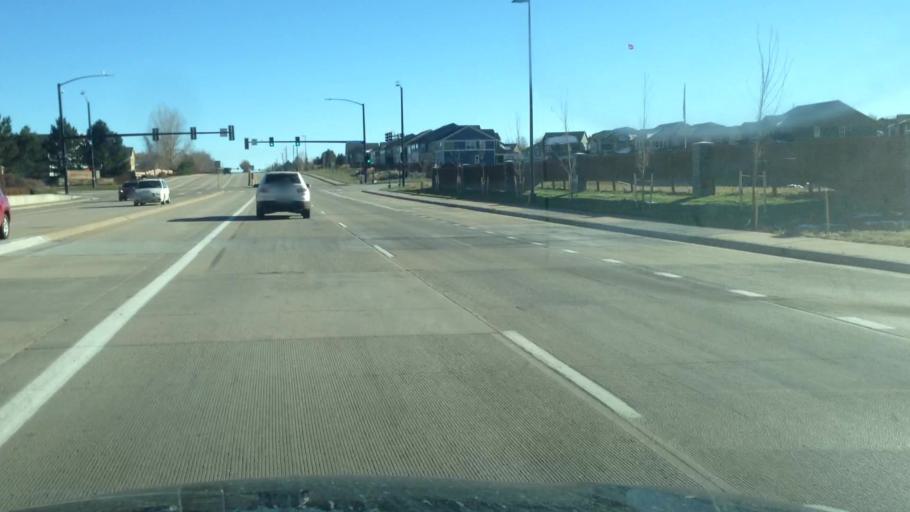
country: US
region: Colorado
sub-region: Arapahoe County
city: Dove Valley
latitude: 39.5689
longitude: -104.8035
